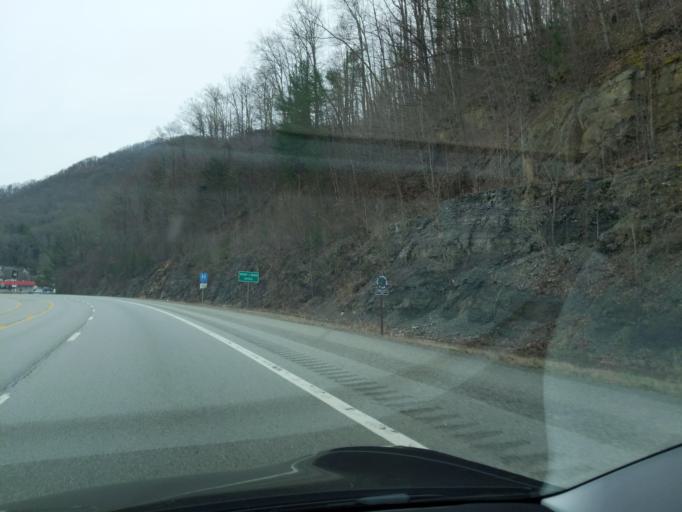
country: US
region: Kentucky
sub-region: Bell County
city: Pineville
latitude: 36.7642
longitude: -83.7131
